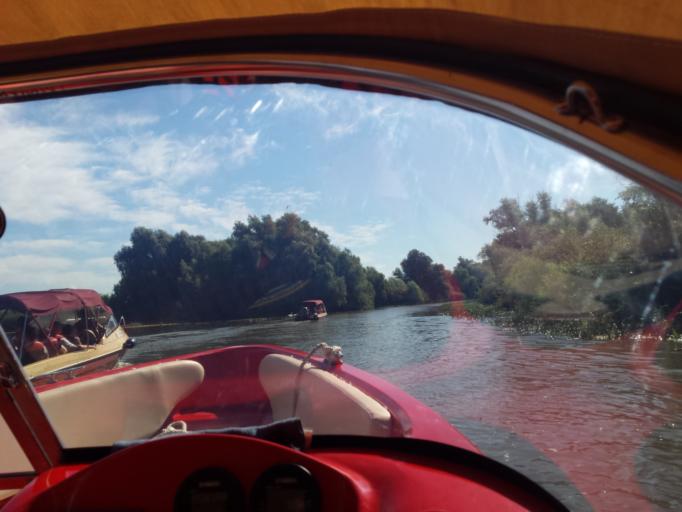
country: RO
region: Tulcea
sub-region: Comuna Pardina
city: Pardina
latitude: 45.2471
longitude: 29.0589
